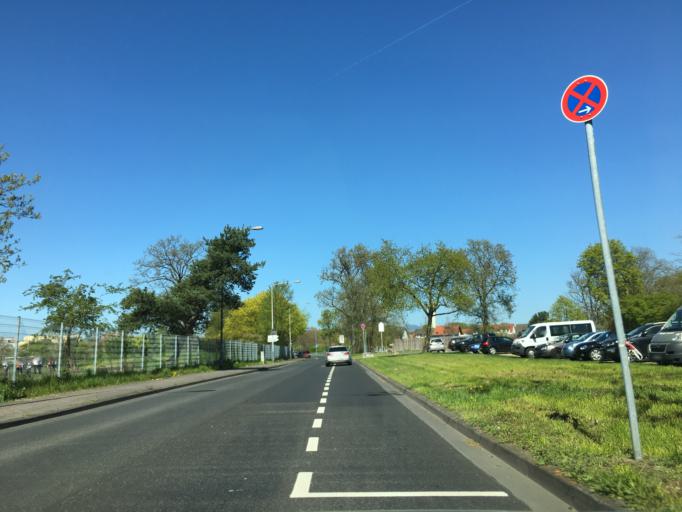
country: DE
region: Hesse
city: Niederrad
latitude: 50.0777
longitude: 8.6118
